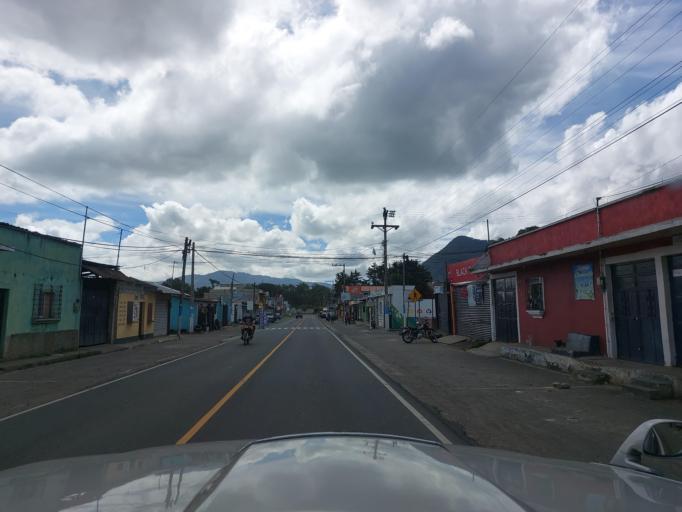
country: GT
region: Chimaltenango
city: Parramos
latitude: 14.6097
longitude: -90.8004
